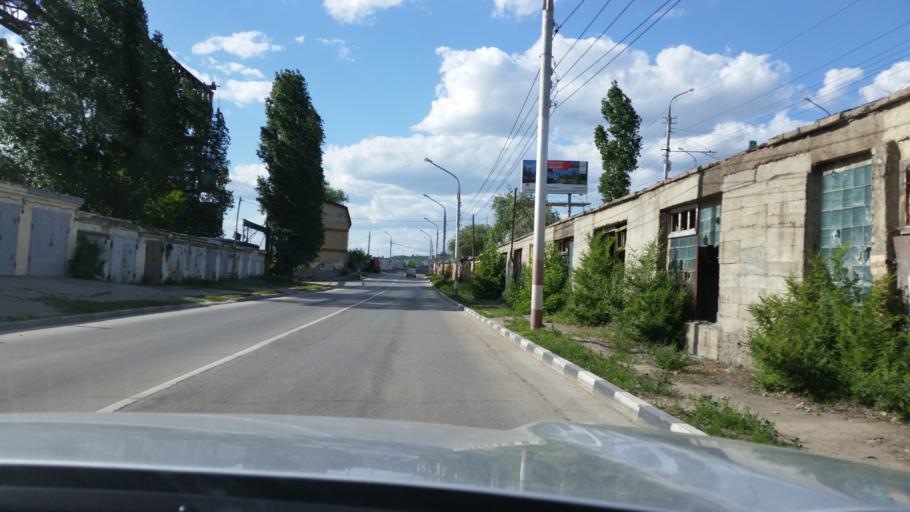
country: RU
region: Saratov
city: Engel's
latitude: 51.5041
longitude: 46.0787
